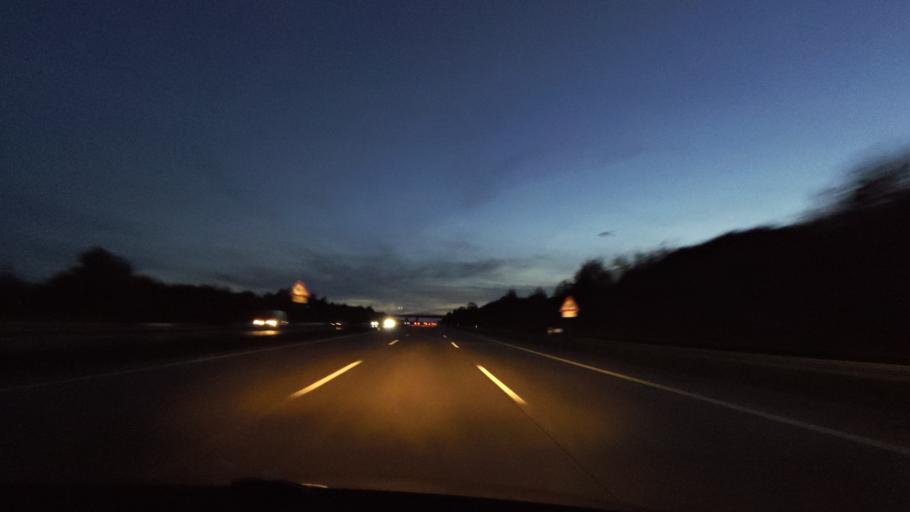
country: DE
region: Thuringia
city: Walpernhain
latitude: 51.0010
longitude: 11.9190
